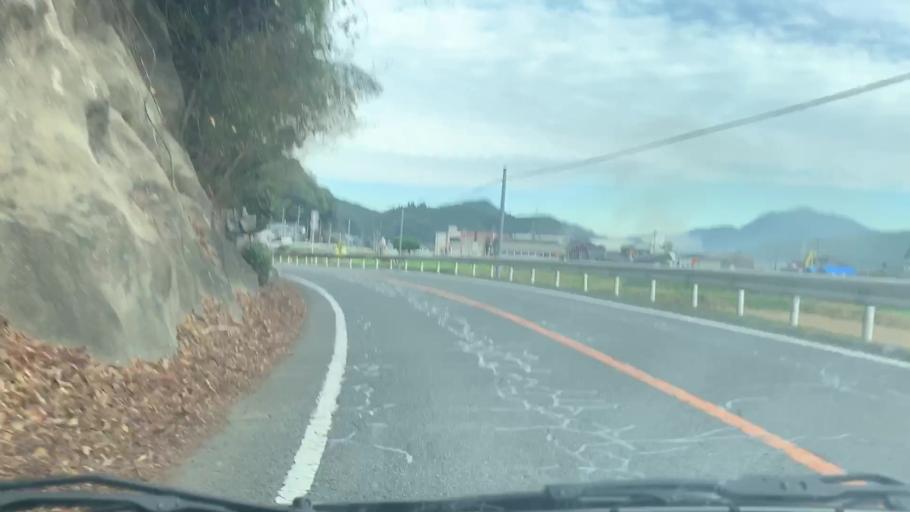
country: JP
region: Saga Prefecture
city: Takeocho-takeo
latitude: 33.2246
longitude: 129.9644
